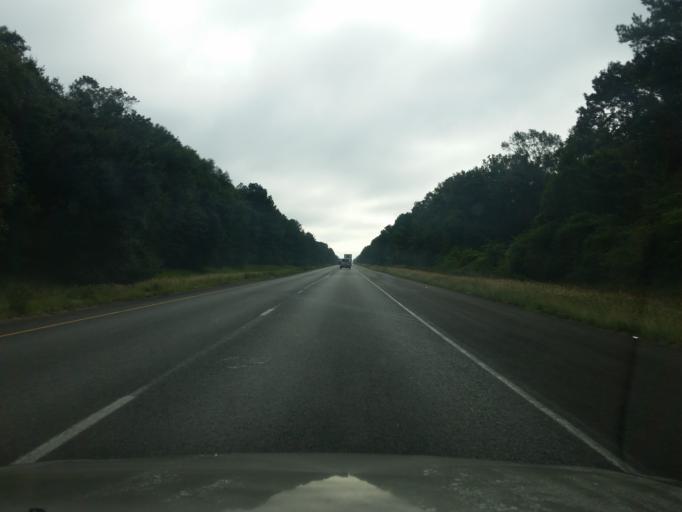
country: US
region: Alabama
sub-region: Baldwin County
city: Spanish Fort
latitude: 30.6620
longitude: -87.8396
